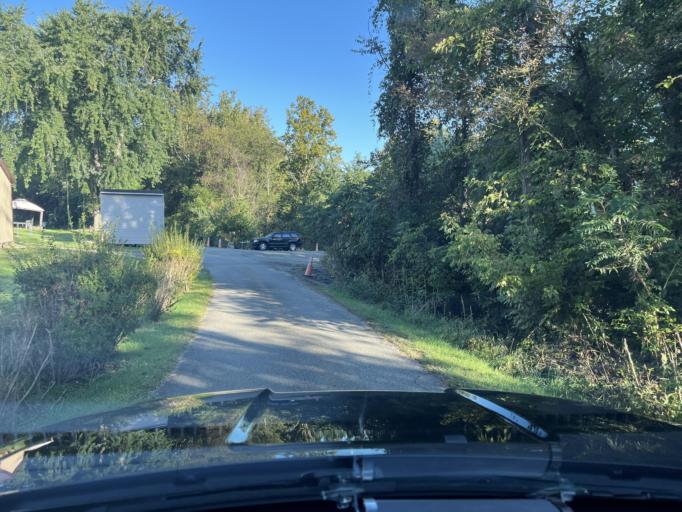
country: US
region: Pennsylvania
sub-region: Fayette County
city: Hopwood
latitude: 39.8773
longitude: -79.7159
